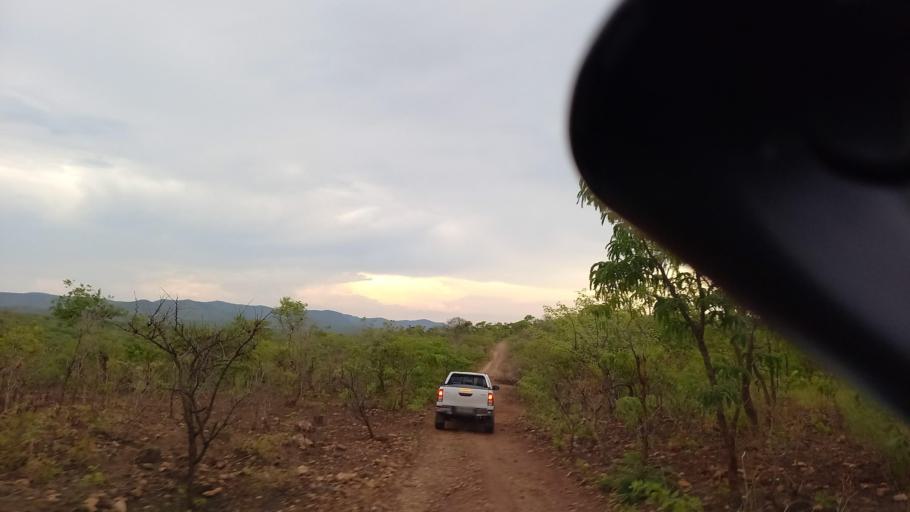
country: ZM
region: Lusaka
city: Kafue
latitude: -16.0469
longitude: 28.3168
